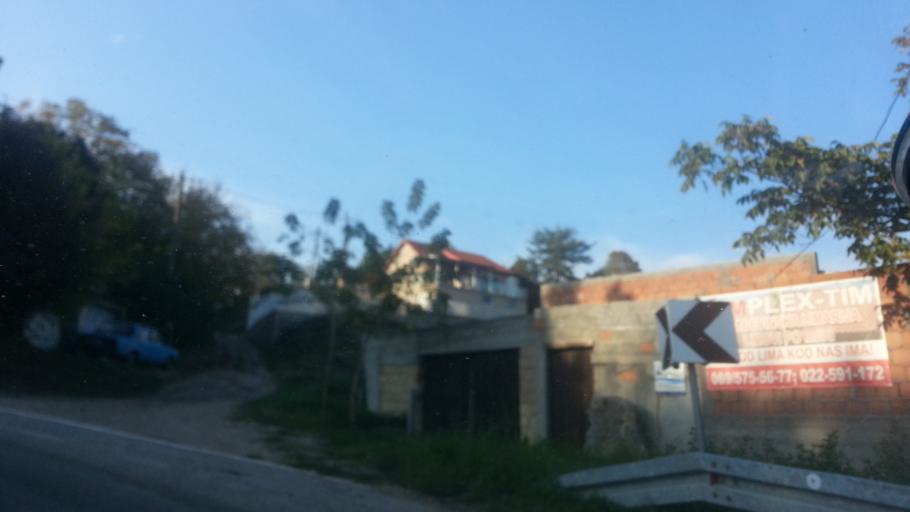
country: RS
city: Novi Slankamen
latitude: 45.1426
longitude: 20.2550
